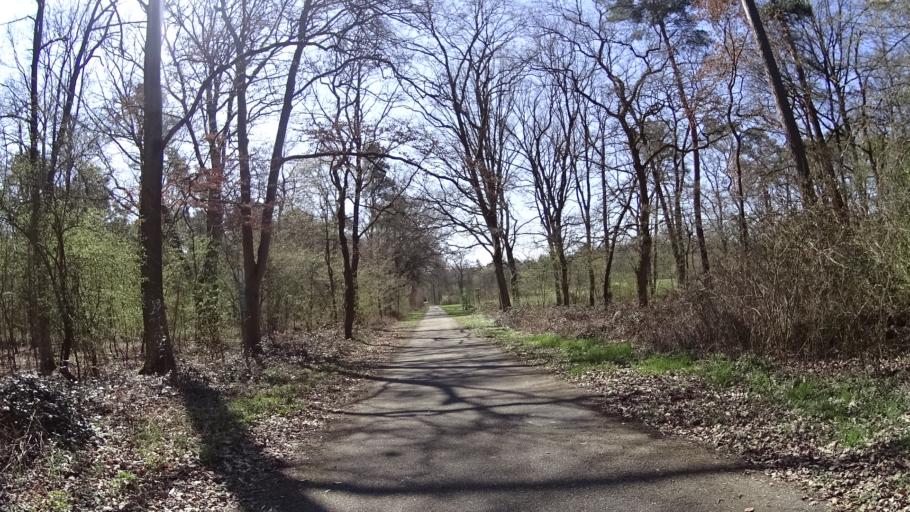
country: DE
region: Baden-Wuerttemberg
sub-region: Karlsruhe Region
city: Bruhl
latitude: 49.4282
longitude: 8.5474
